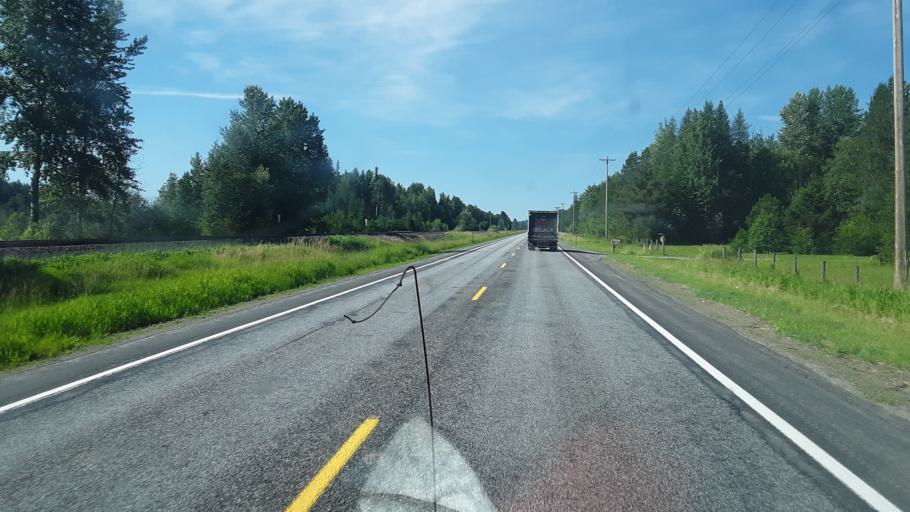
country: US
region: Idaho
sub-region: Bonner County
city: Ponderay
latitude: 48.4721
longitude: -116.4672
